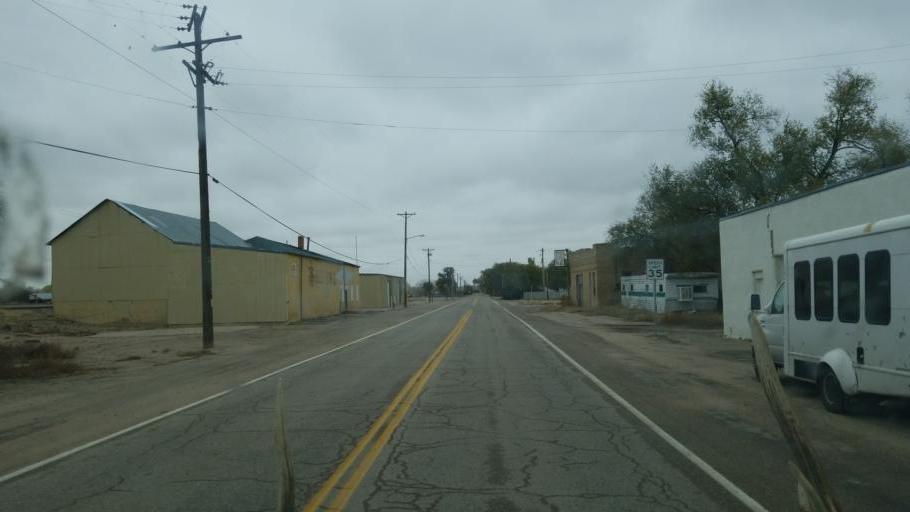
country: US
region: Colorado
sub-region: Otero County
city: Fowler
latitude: 38.2482
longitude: -104.2569
